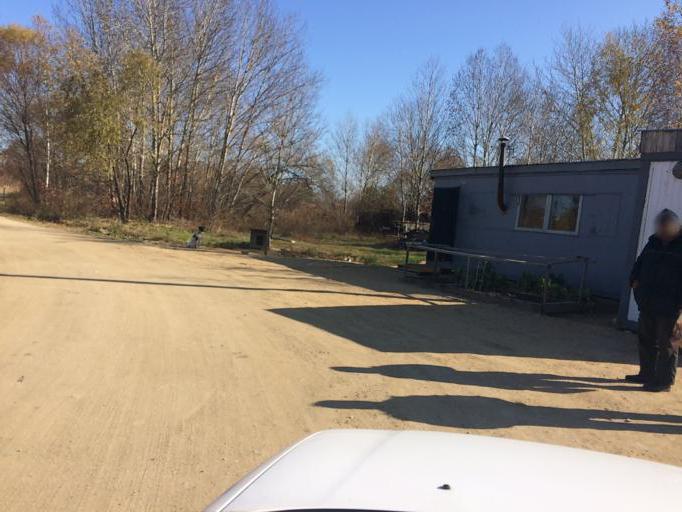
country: RU
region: Primorskiy
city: Dal'nerechensk
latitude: 45.9113
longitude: 133.8076
